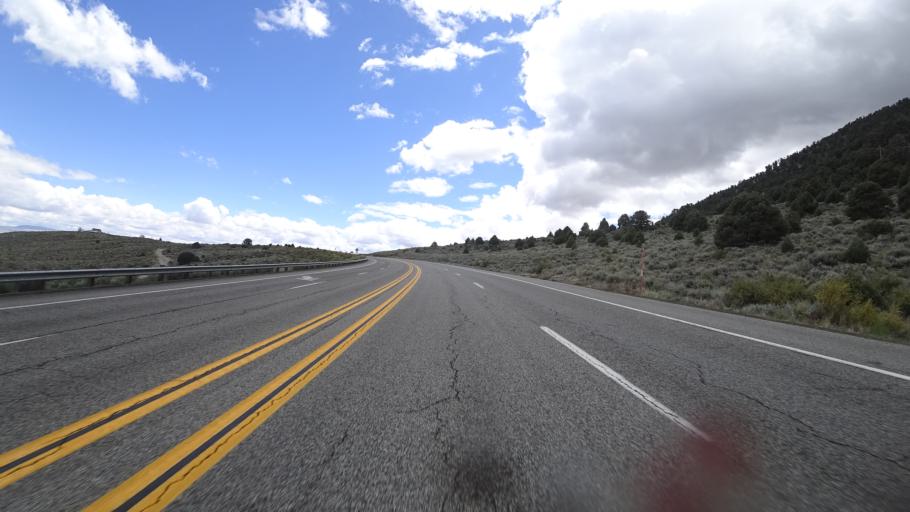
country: US
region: California
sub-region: Mono County
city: Bridgeport
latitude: 37.9675
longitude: -119.1302
